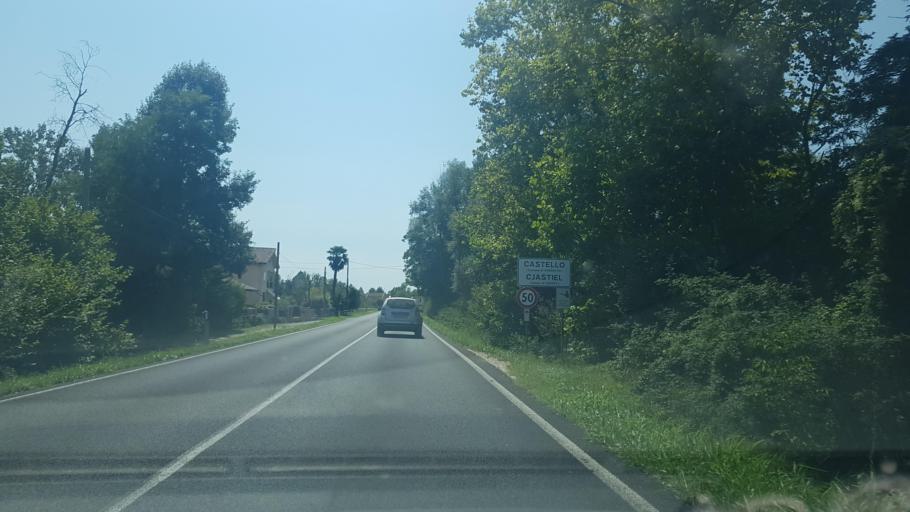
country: IT
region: Friuli Venezia Giulia
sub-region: Provincia di Udine
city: Porpetto
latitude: 45.8776
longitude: 13.2272
